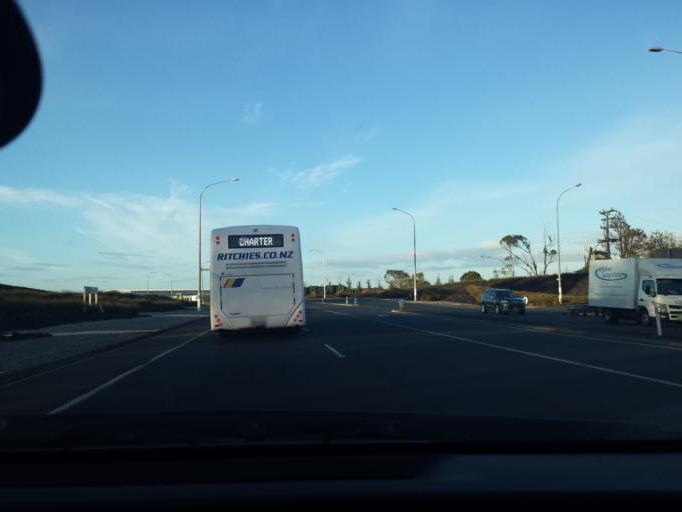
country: NZ
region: Auckland
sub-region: Auckland
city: Mangere
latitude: -36.9935
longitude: 174.7864
